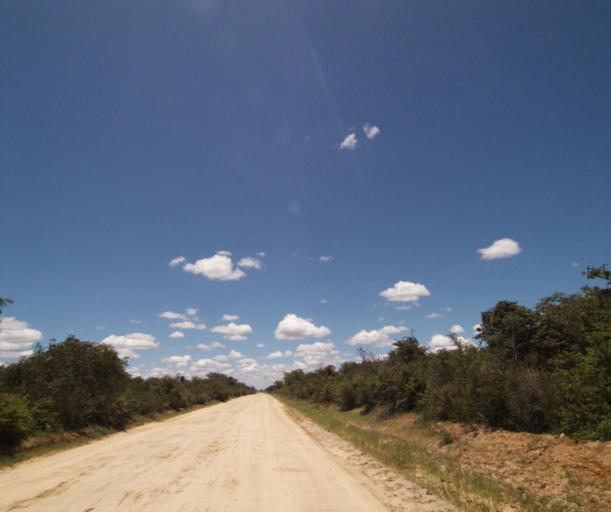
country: BR
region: Bahia
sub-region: Carinhanha
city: Carinhanha
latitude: -14.2328
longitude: -43.8616
